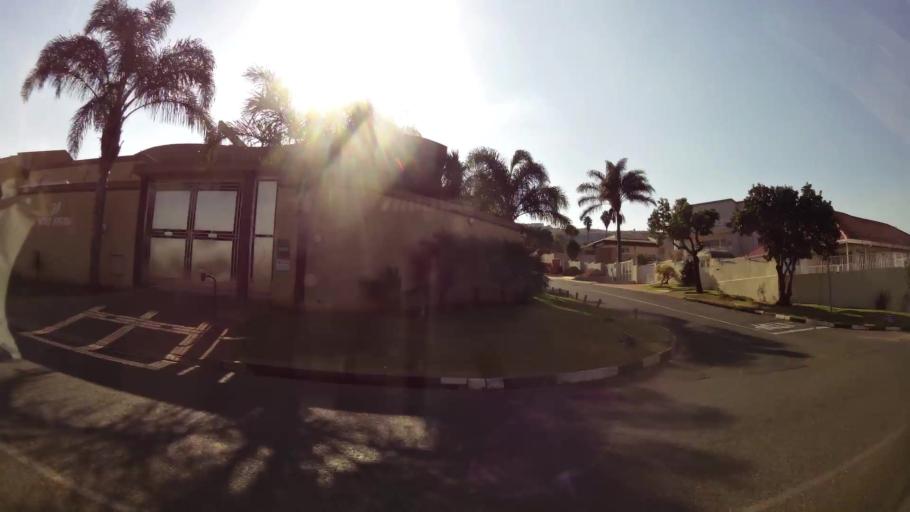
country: ZA
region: Gauteng
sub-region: City of Johannesburg Metropolitan Municipality
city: Johannesburg
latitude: -26.1752
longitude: 28.1106
